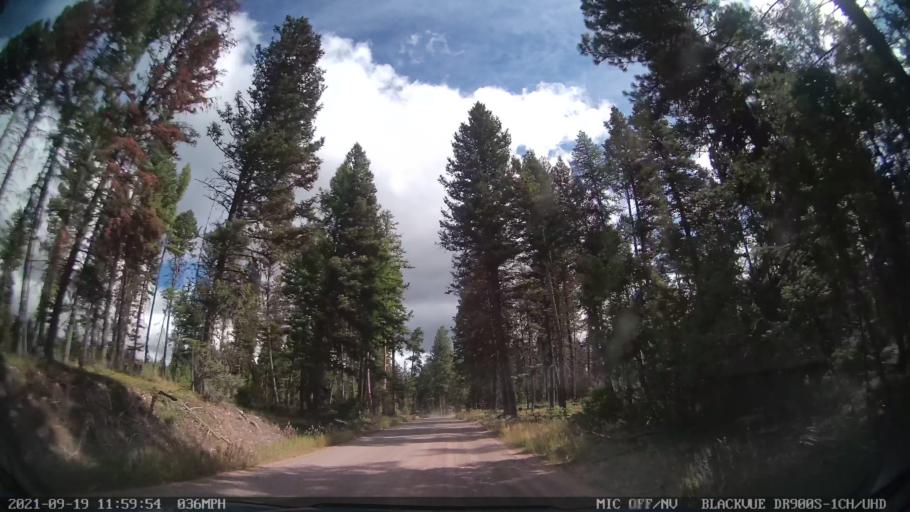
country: US
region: Montana
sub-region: Missoula County
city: Seeley Lake
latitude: 47.1865
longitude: -113.4722
